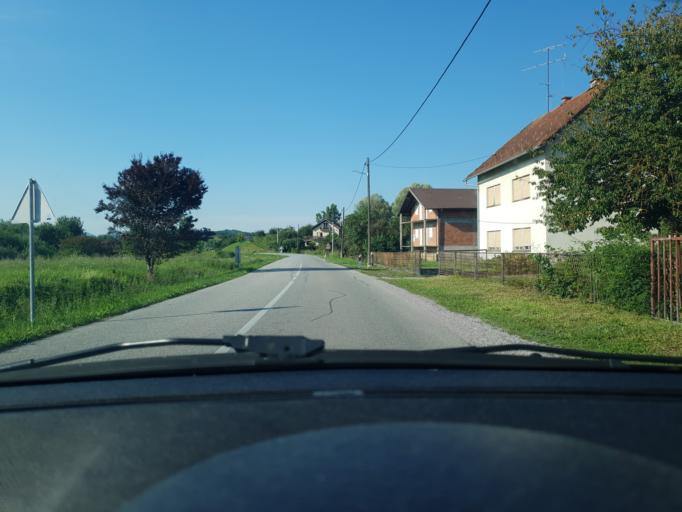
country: HR
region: Krapinsko-Zagorska
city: Oroslavje
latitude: 46.0017
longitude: 15.9302
